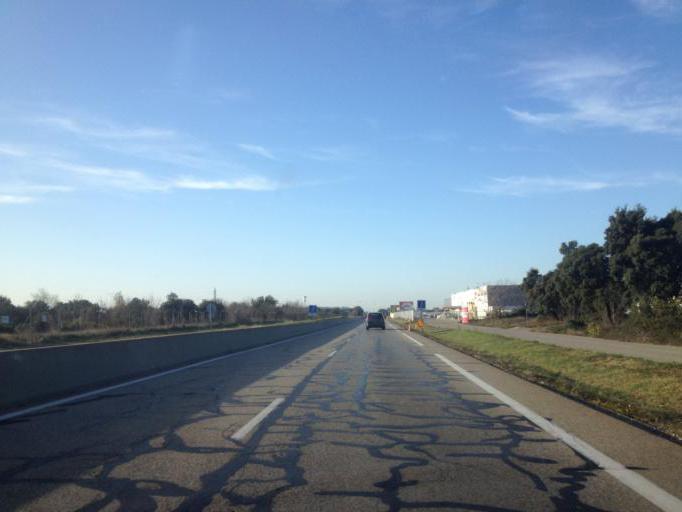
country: FR
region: Provence-Alpes-Cote d'Azur
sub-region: Departement du Vaucluse
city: Orange
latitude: 44.1148
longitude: 4.8421
